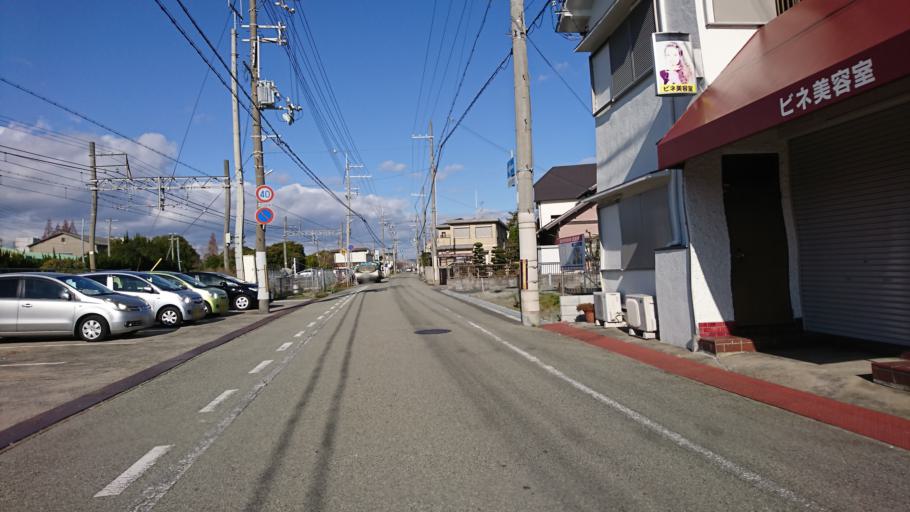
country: JP
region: Hyogo
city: Kakogawacho-honmachi
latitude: 34.7609
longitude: 134.7909
